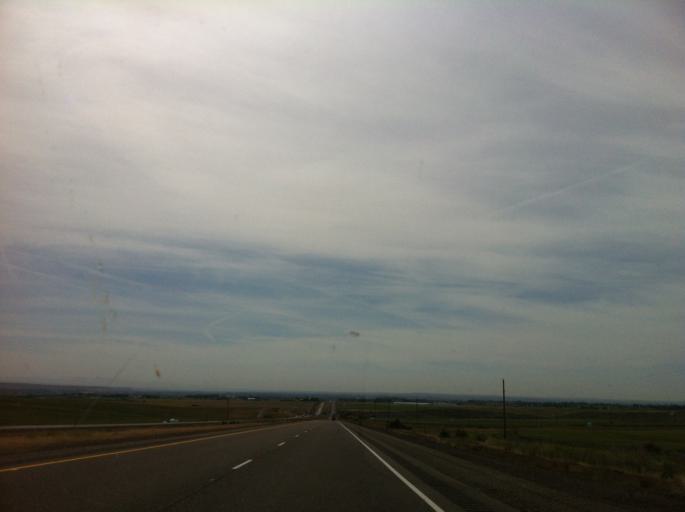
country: US
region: Oregon
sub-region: Malheur County
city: Ontario
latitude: 44.1092
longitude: -117.0530
